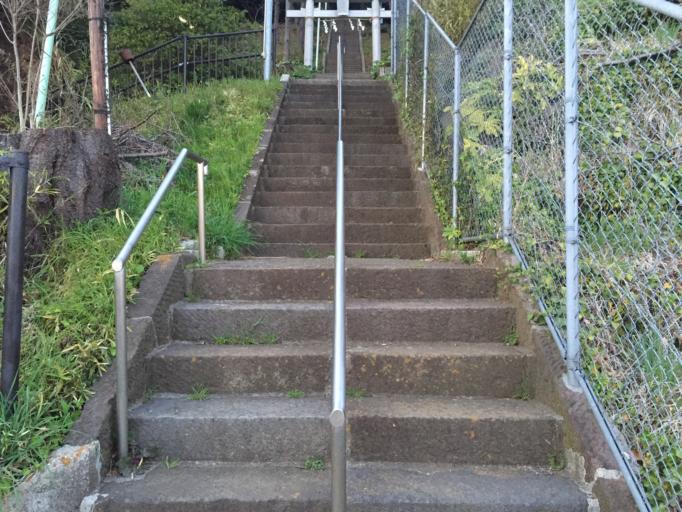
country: JP
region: Kanagawa
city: Yokohama
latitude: 35.3971
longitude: 139.6127
